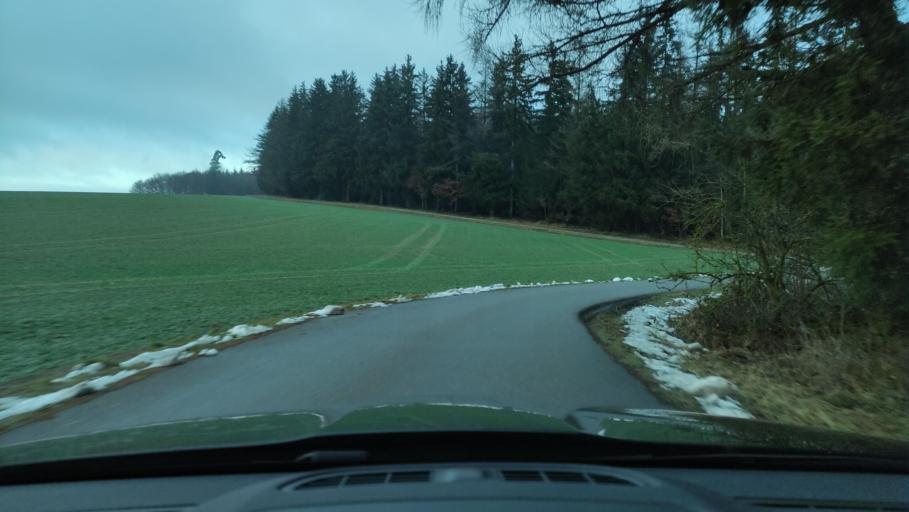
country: DE
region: Bavaria
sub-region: Swabia
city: Deisenhausen
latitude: 48.2801
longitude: 10.3441
